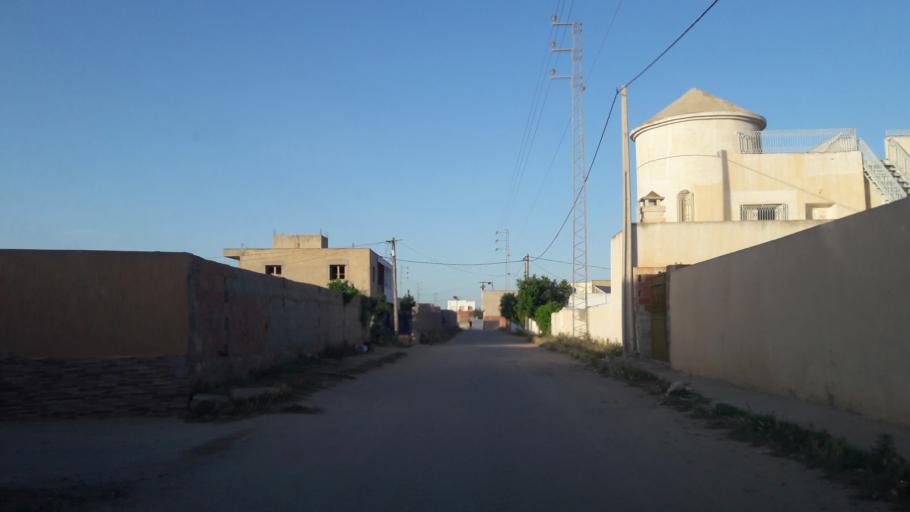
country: TN
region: Safaqis
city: Al Qarmadah
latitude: 34.8192
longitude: 10.7441
